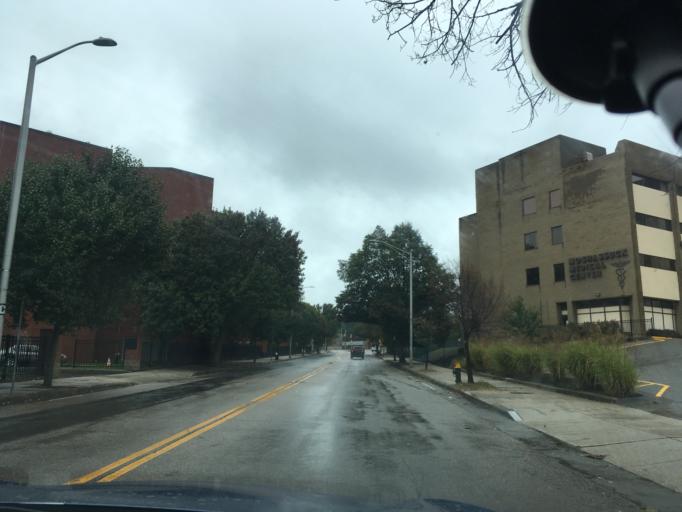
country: US
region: Rhode Island
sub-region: Providence County
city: Providence
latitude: 41.8367
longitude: -71.4115
